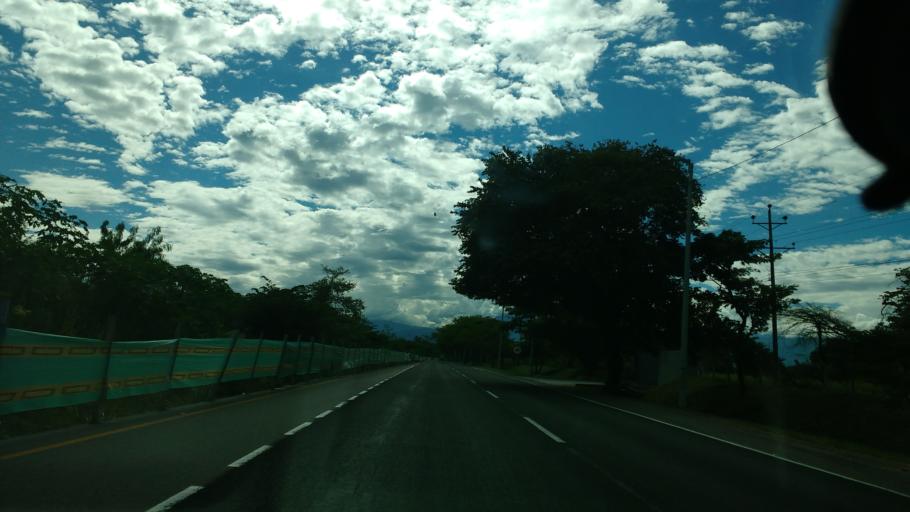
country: CO
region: Tolima
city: Valle de San Juan
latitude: 4.3231
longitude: -75.0702
